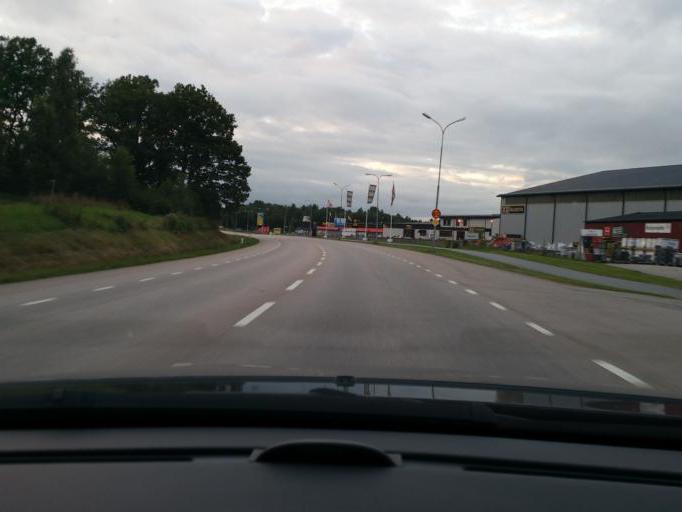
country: SE
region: Kronoberg
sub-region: Alvesta Kommun
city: Alvesta
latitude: 56.9077
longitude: 14.5569
